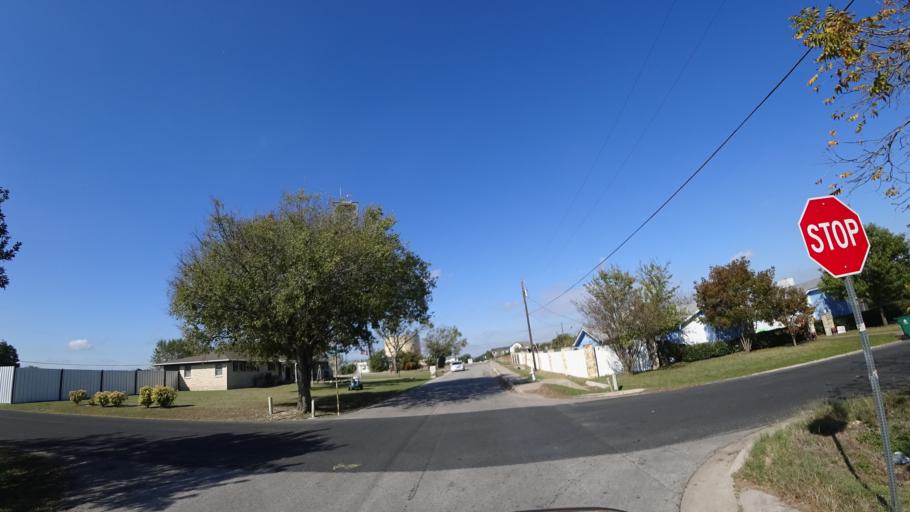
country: US
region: Texas
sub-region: Travis County
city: Windemere
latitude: 30.4441
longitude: -97.6519
